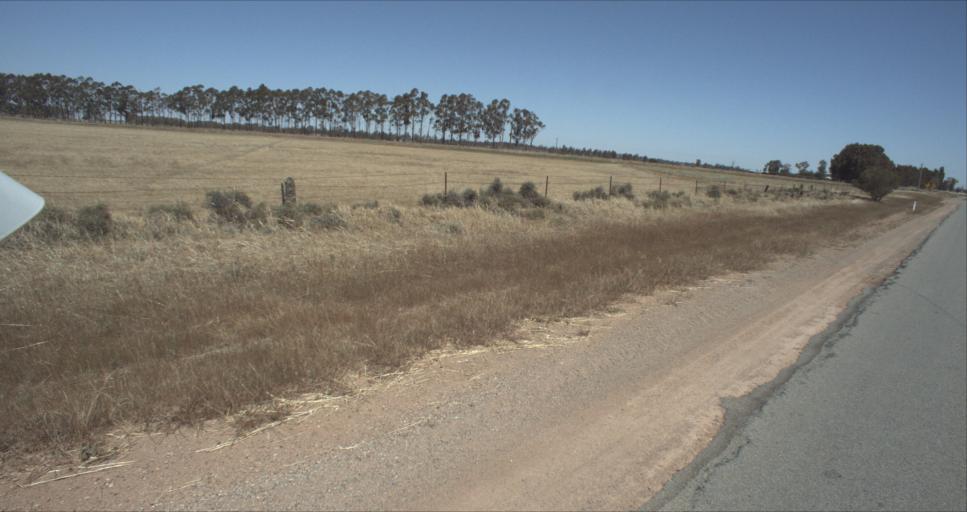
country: AU
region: New South Wales
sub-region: Leeton
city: Leeton
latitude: -34.5344
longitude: 146.4462
